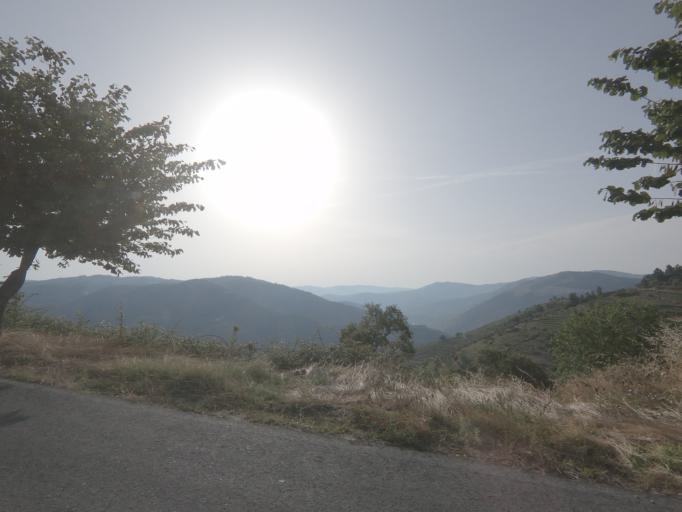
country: PT
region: Vila Real
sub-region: Sabrosa
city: Sabrosa
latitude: 41.2066
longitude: -7.5279
